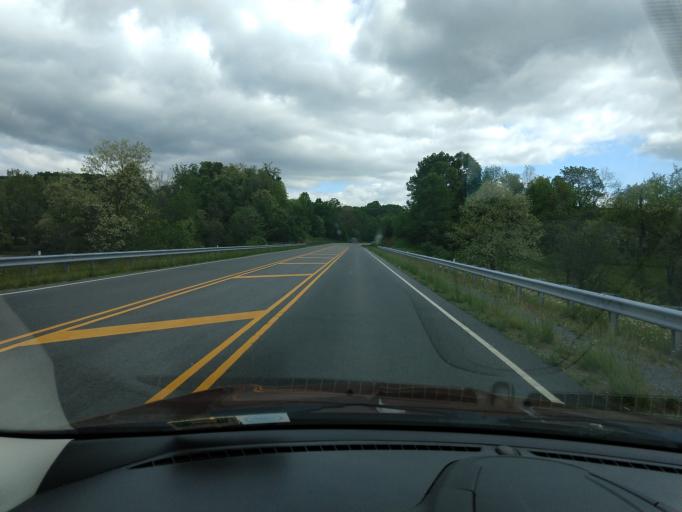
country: US
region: Virginia
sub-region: Wythe County
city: Wytheville
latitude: 36.8894
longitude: -80.9752
